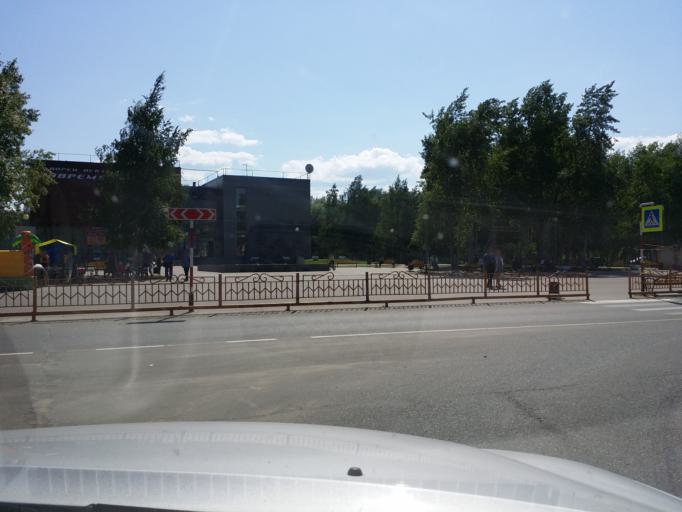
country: RU
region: Tomsk
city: Strezhevoy
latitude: 60.7268
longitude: 77.6045
